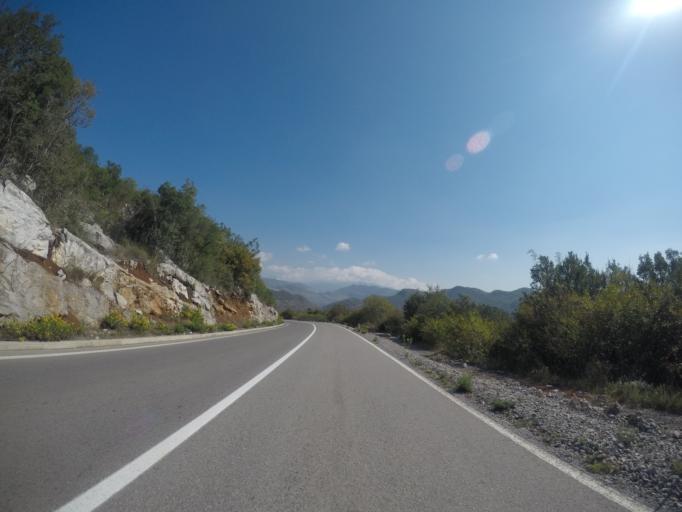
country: AL
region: Shkoder
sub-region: Rrethi i Malesia e Madhe
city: Hot
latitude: 42.3212
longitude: 19.4011
